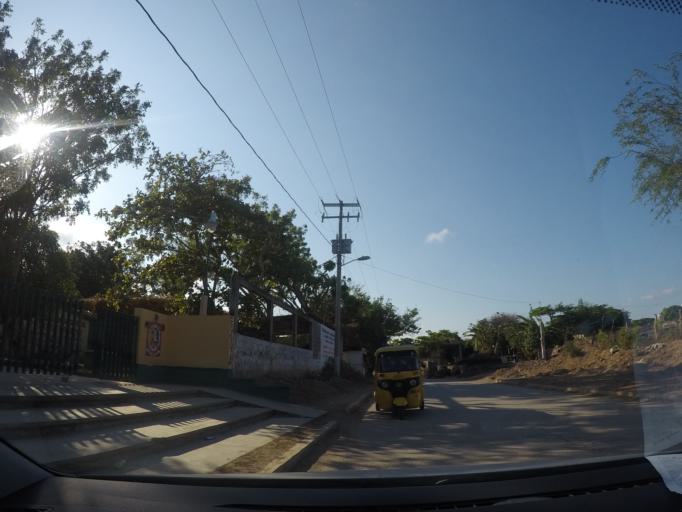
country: MX
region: Oaxaca
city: Juchitan de Zaragoza
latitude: 16.4181
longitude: -95.0222
